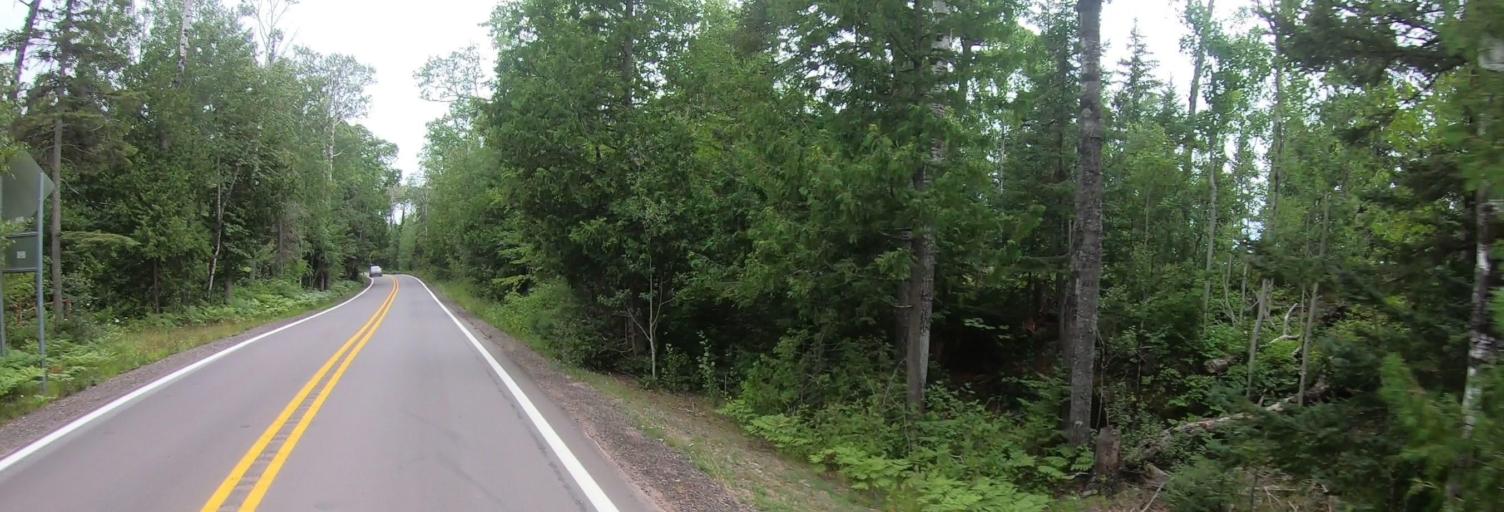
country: US
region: Michigan
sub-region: Keweenaw County
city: Eagle River
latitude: 47.4628
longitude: -88.0732
